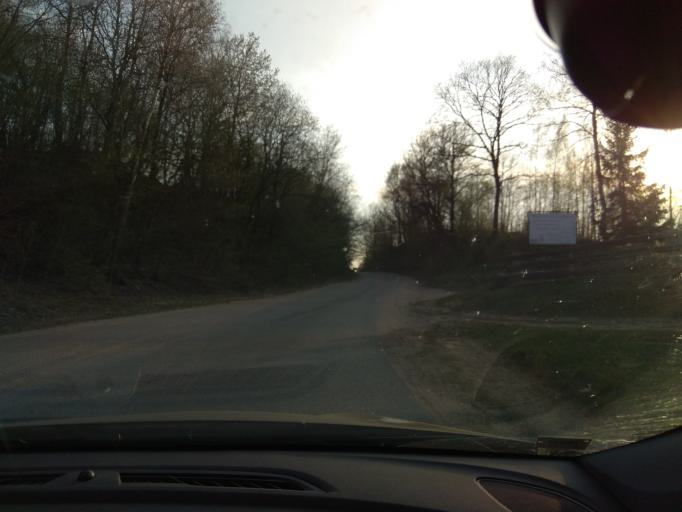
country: LT
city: Baltoji Voke
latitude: 54.5931
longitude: 25.1726
